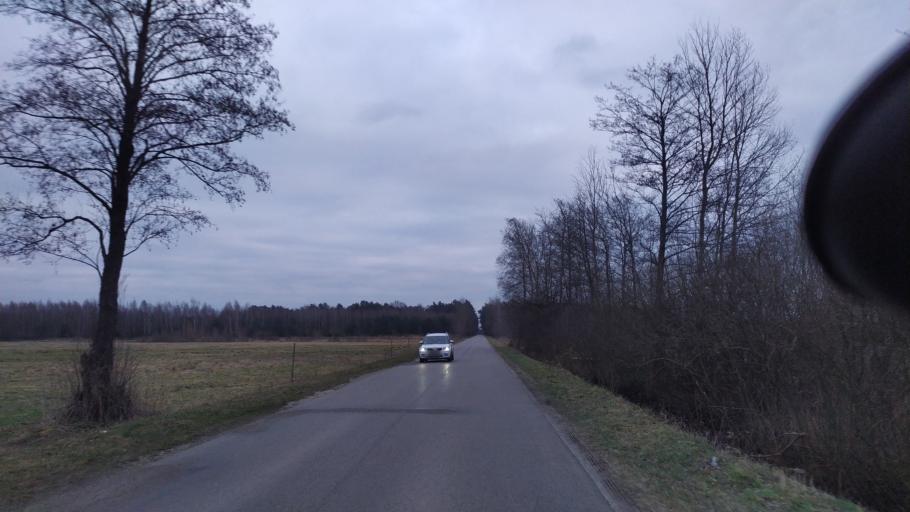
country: PL
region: Lublin Voivodeship
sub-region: Powiat lubartowski
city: Abramow
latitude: 51.4244
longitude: 22.3159
